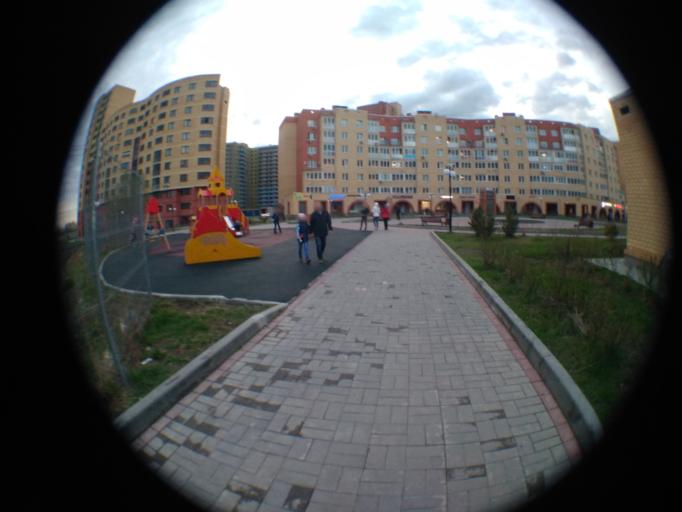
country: RU
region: Moskovskaya
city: Bykovo
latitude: 55.6029
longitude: 38.0865
